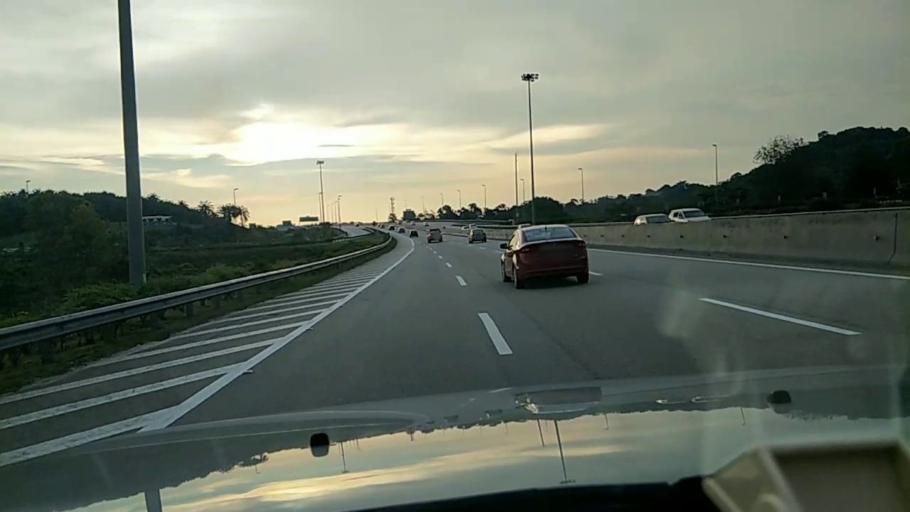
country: MY
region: Selangor
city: Kuang
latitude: 3.2700
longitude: 101.5444
